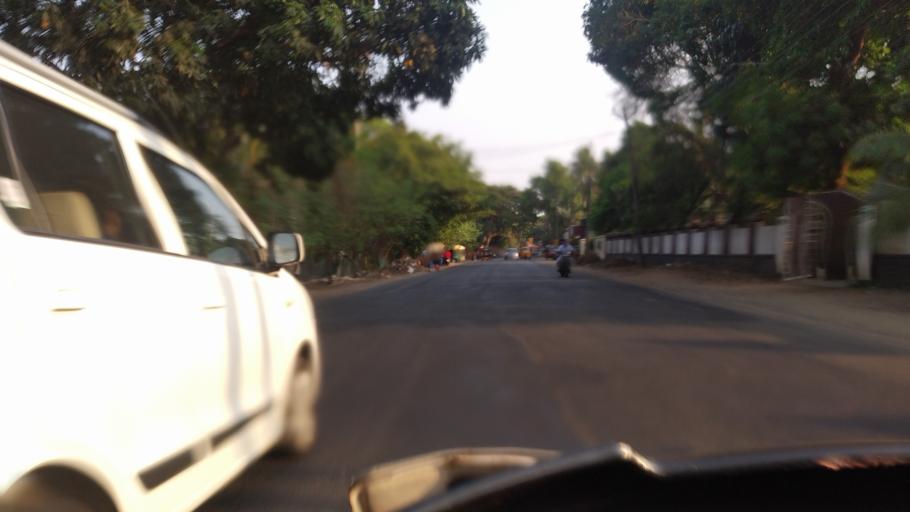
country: IN
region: Kerala
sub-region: Thrissur District
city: Thanniyam
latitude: 10.3867
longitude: 76.1198
